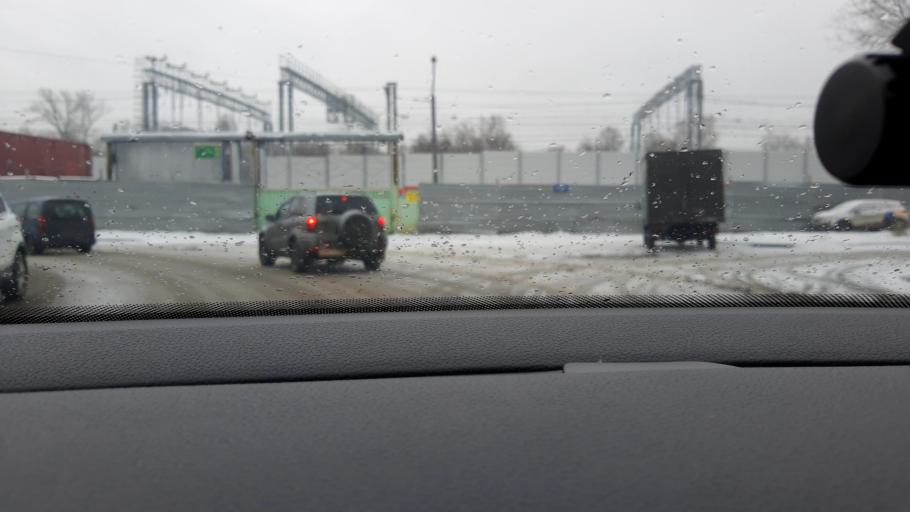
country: RU
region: Moskovskaya
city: Novogireyevo
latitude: 55.7432
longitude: 37.8099
